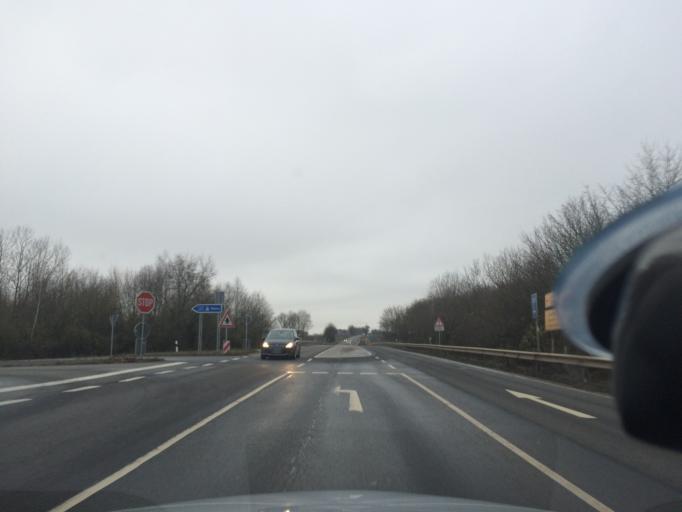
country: DE
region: Rheinland-Pfalz
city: Worrstadt
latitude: 49.8415
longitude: 8.1465
